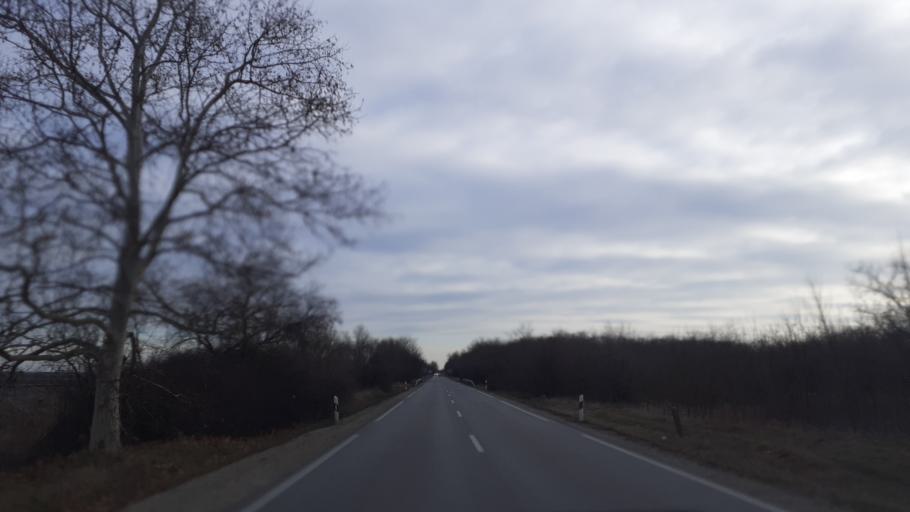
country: HU
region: Fejer
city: Sarkeresztur
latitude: 46.9537
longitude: 18.5865
